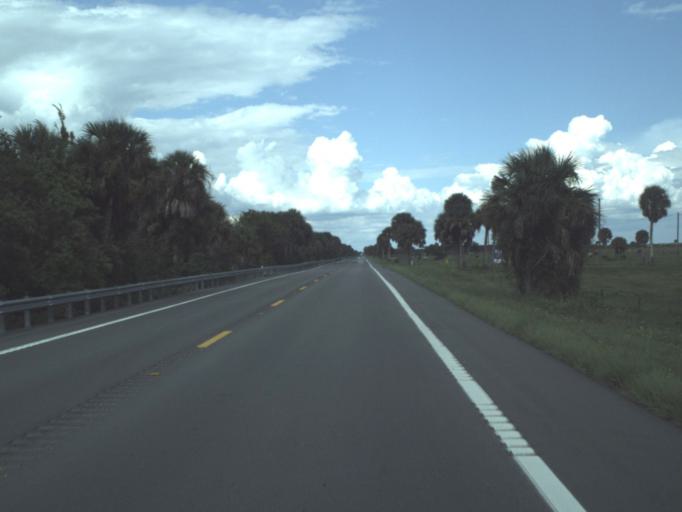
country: US
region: Florida
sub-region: Glades County
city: Buckhead Ridge
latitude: 27.0891
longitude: -80.9626
